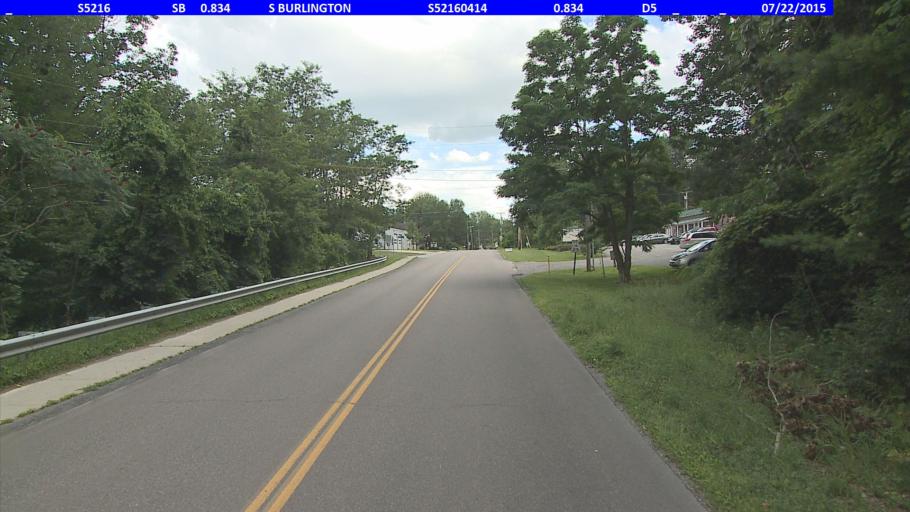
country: US
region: Vermont
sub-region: Chittenden County
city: South Burlington
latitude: 44.4781
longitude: -73.1760
